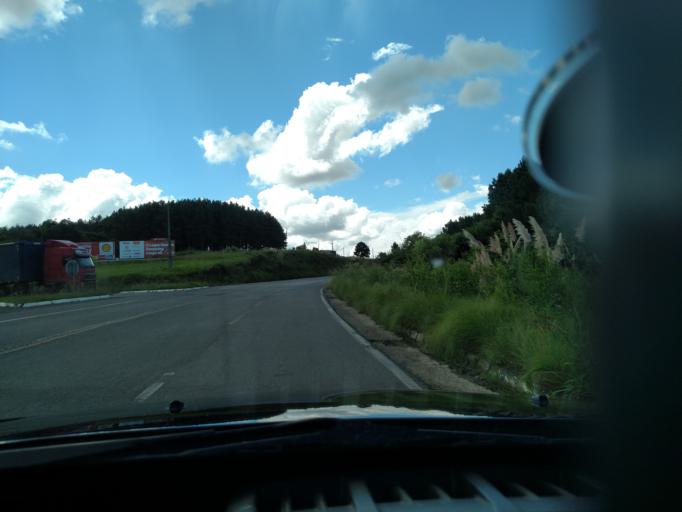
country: BR
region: Santa Catarina
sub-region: Lages
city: Lages
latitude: -27.8288
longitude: -50.2479
